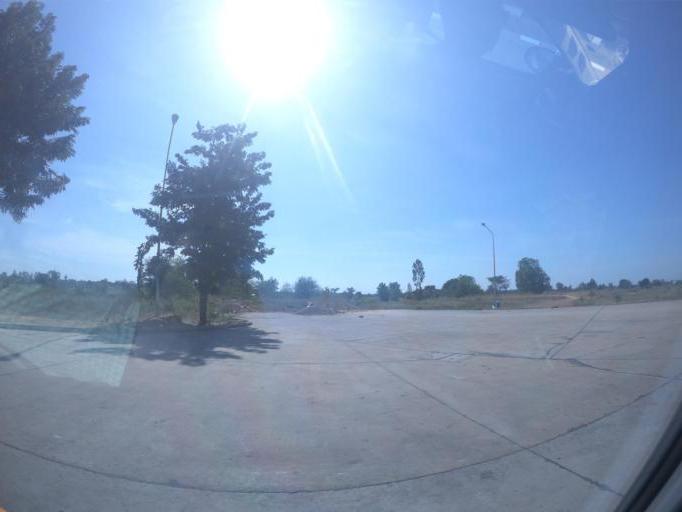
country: TH
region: Khon Kaen
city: Khon Kaen
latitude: 16.3890
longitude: 102.8028
